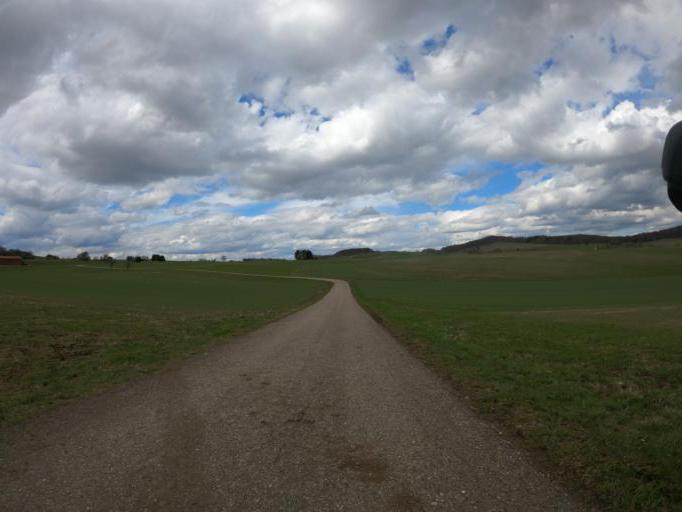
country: DE
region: Baden-Wuerttemberg
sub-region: Tuebingen Region
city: Pfullingen
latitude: 48.3882
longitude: 9.1977
